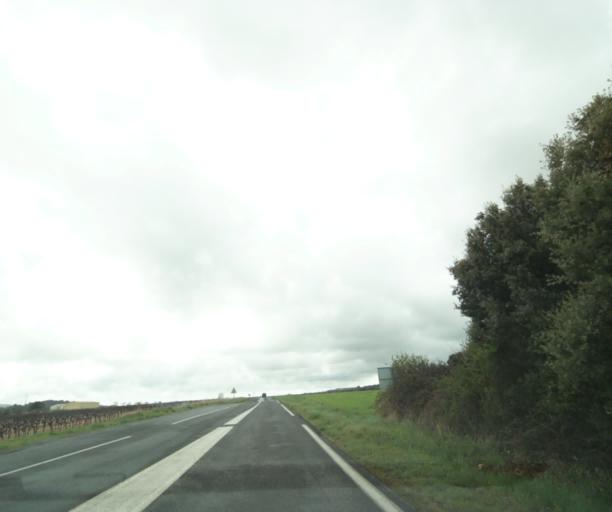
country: FR
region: Languedoc-Roussillon
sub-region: Departement de l'Herault
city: Cournonsec
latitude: 43.5395
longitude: 3.6993
